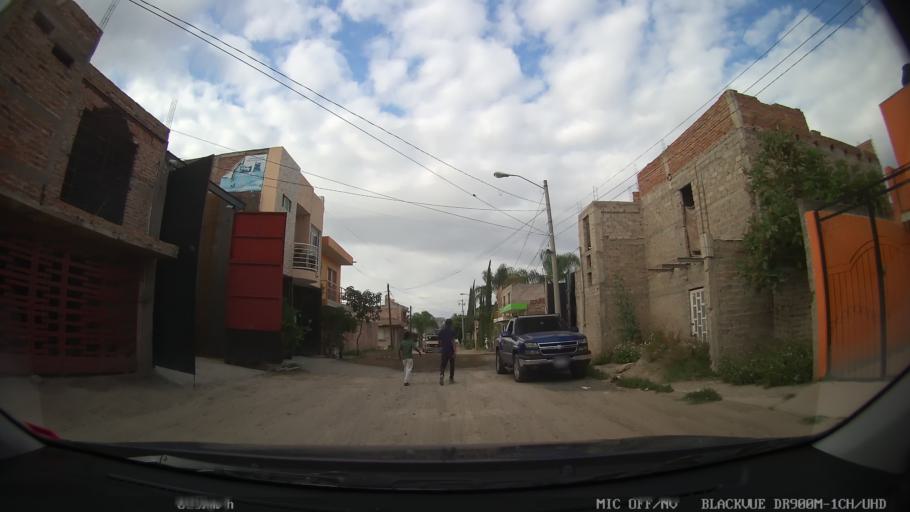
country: MX
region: Jalisco
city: Tonala
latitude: 20.6680
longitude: -103.2369
